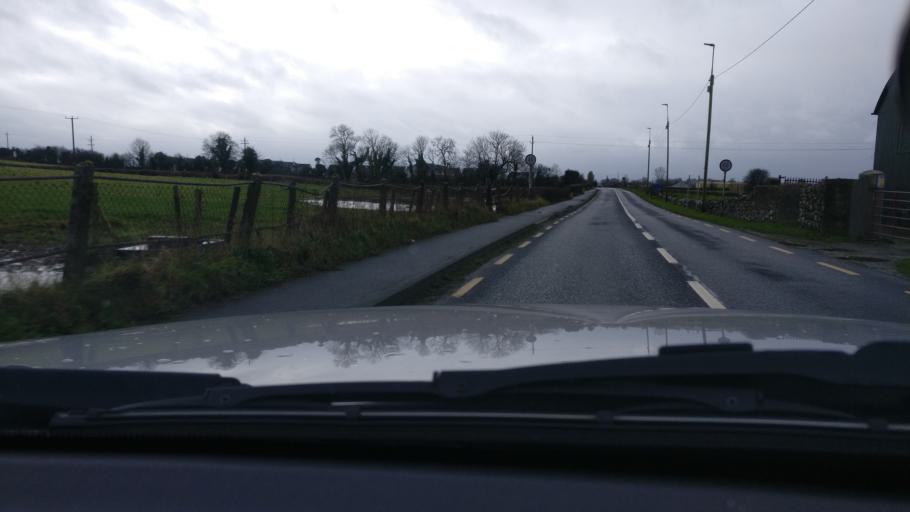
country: IE
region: Leinster
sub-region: An Longfort
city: Ballymahon
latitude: 53.5584
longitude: -7.7655
